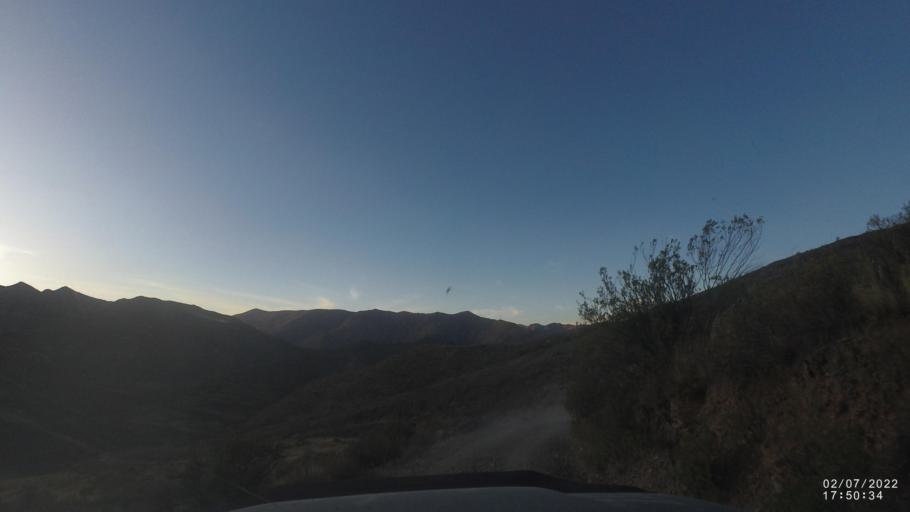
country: BO
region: Cochabamba
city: Irpa Irpa
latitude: -17.8488
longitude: -66.6173
